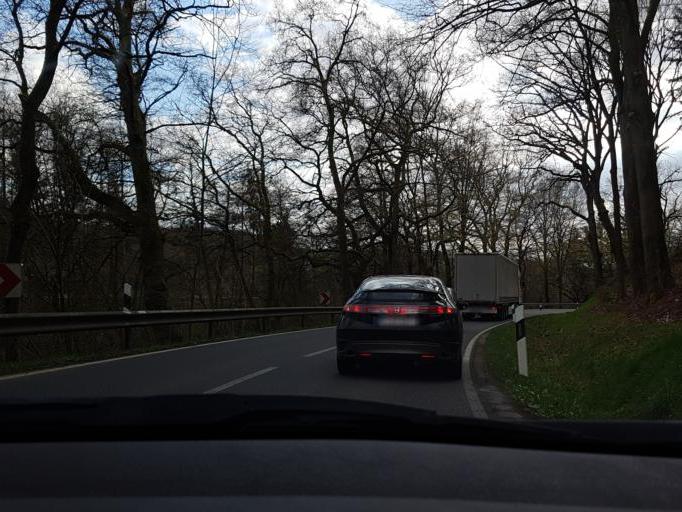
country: DE
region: Lower Saxony
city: Bodenfelde
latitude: 51.6279
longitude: 9.5791
